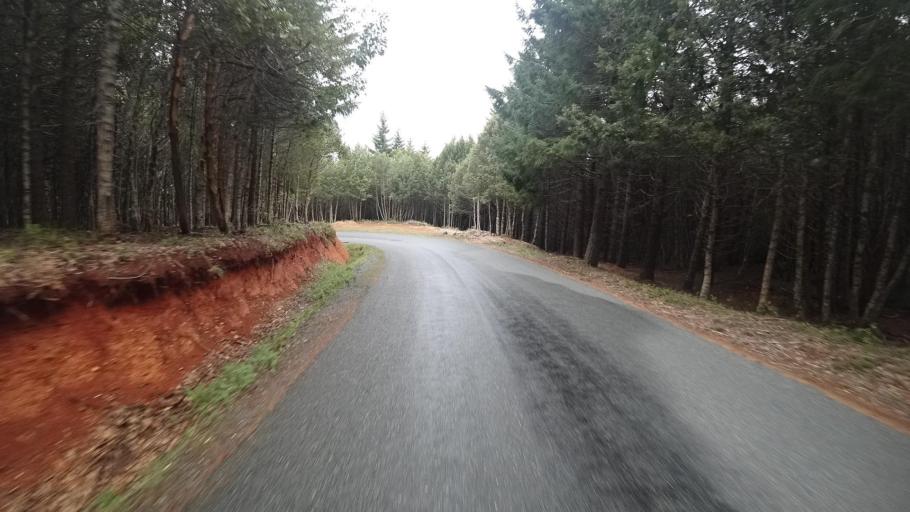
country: US
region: California
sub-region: Humboldt County
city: Willow Creek
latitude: 41.2003
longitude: -123.7939
